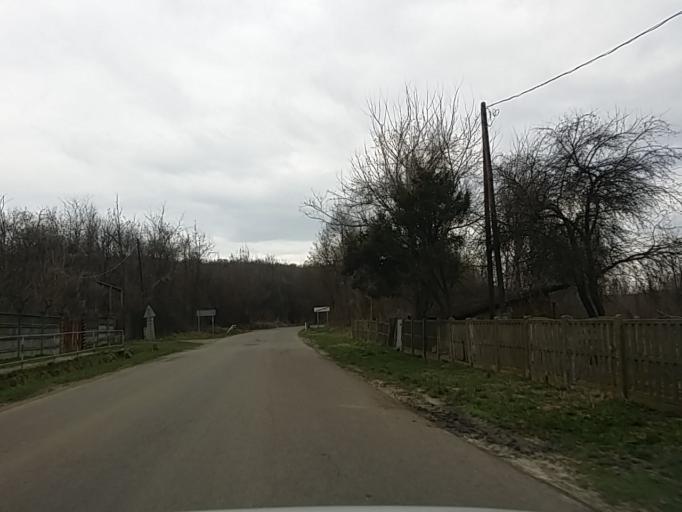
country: HU
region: Heves
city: Verpelet
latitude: 47.8791
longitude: 20.1969
